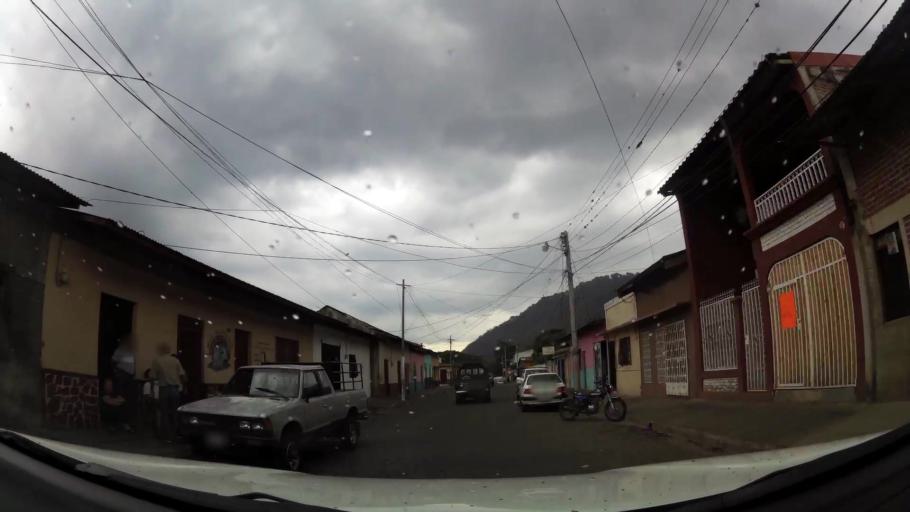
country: NI
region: Jinotega
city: Jinotega
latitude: 13.0964
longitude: -86.0036
